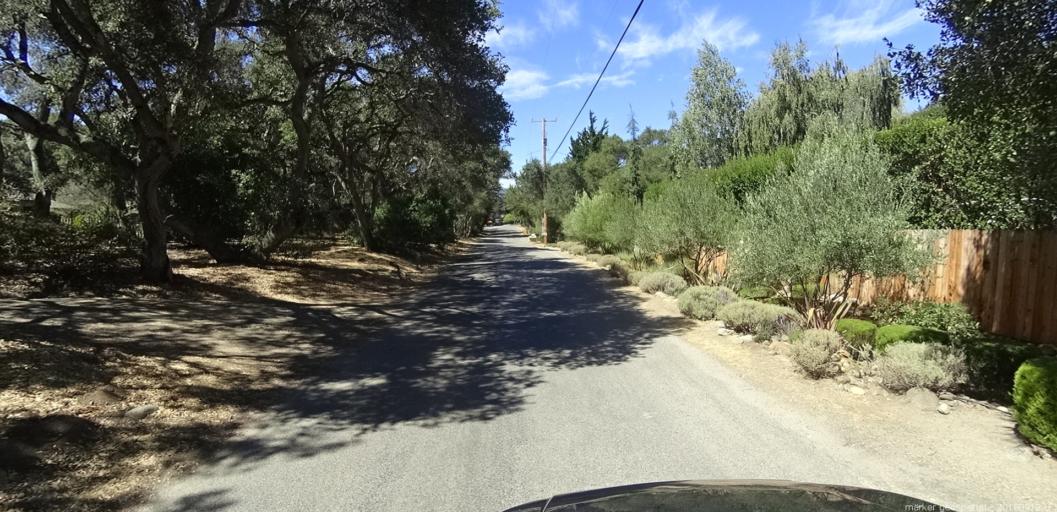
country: US
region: California
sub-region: Monterey County
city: Carmel Valley Village
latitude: 36.4773
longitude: -121.7252
